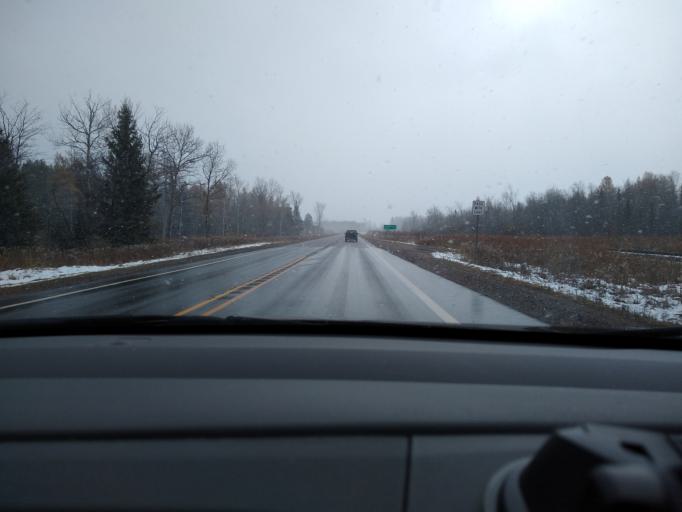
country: US
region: Wisconsin
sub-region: Florence County
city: Florence
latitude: 46.0850
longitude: -88.0756
